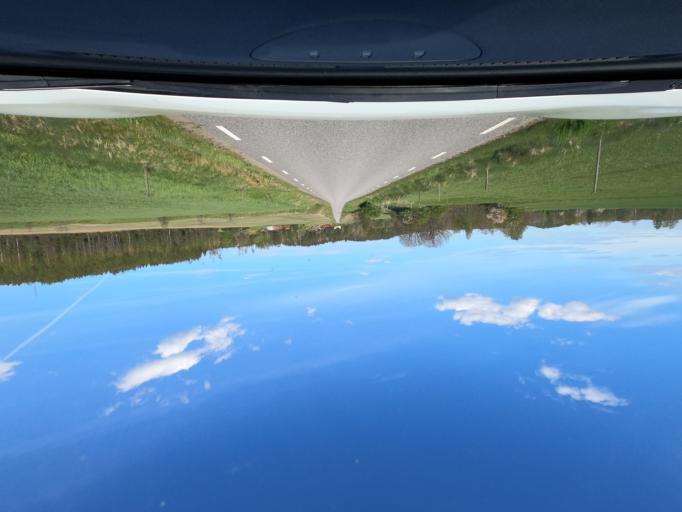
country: SE
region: Vaestra Goetaland
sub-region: Harryda Kommun
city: Ravlanda
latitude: 57.6113
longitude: 12.4884
